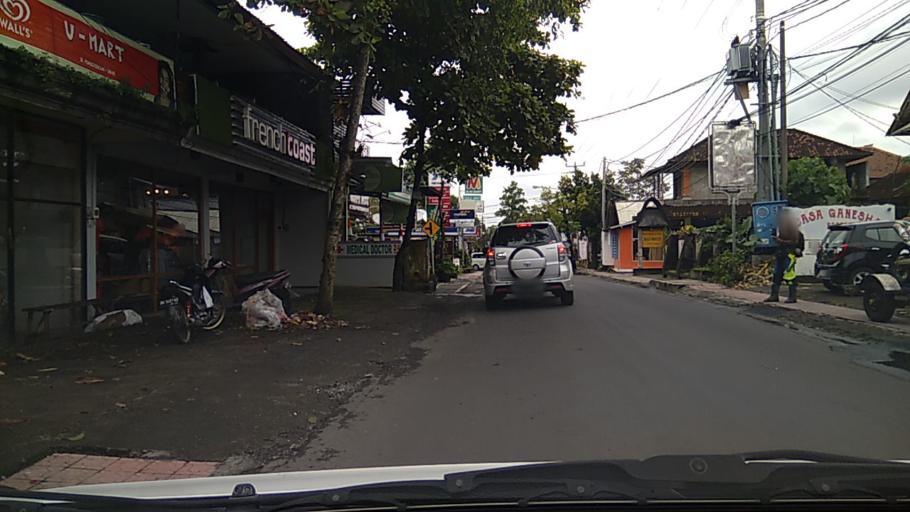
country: ID
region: Bali
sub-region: Kabupaten Gianyar
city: Ubud
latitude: -8.5238
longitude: 115.2634
